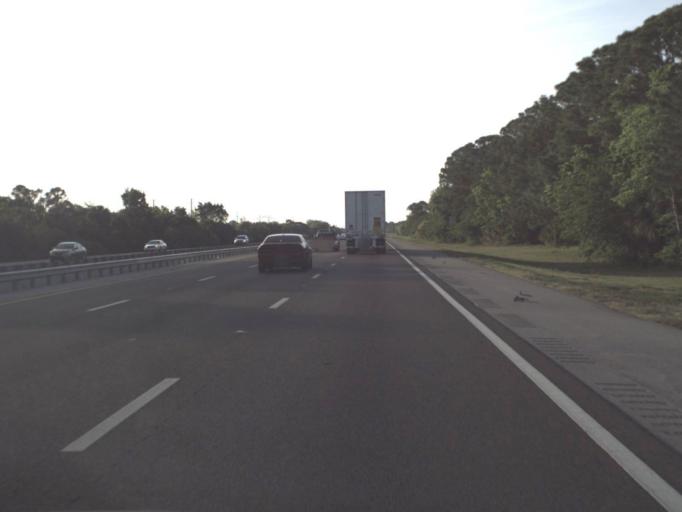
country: US
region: Florida
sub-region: Brevard County
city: Port Saint John
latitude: 28.4917
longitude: -80.8305
